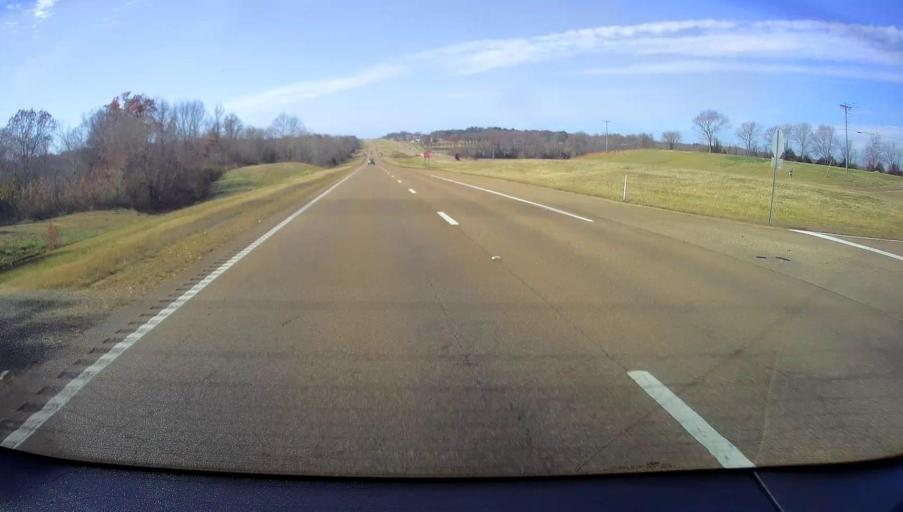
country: US
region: Mississippi
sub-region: Marshall County
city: Holly Springs
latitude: 34.9461
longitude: -89.3705
